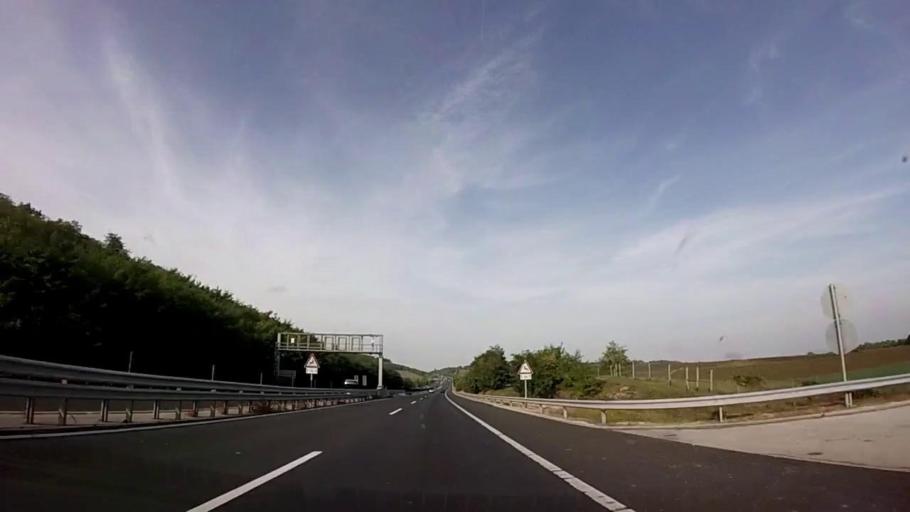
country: HU
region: Somogy
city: Balatonfoldvar
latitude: 46.8198
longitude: 17.8881
